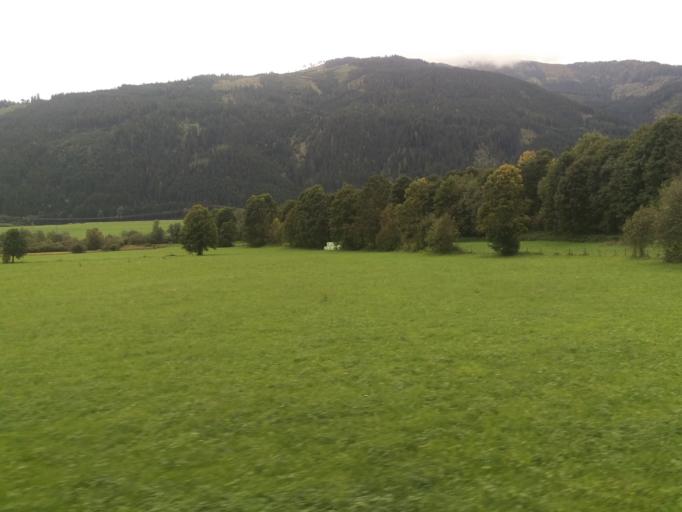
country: AT
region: Salzburg
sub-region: Politischer Bezirk Zell am See
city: Stuhlfelden
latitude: 47.2864
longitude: 12.5370
